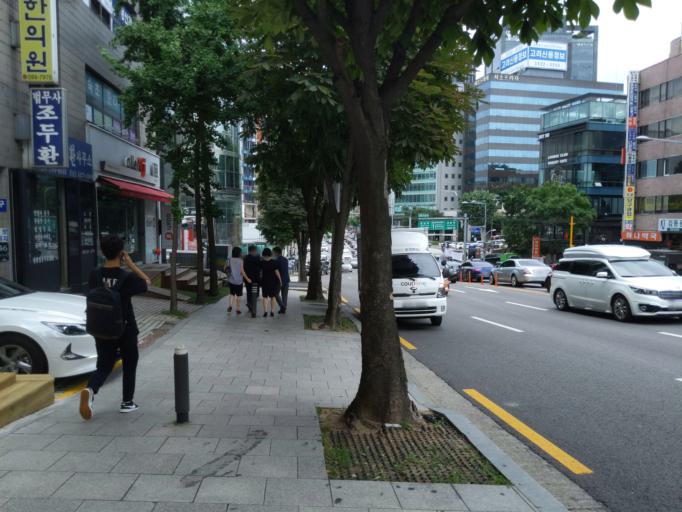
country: KR
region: Seoul
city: Seoul
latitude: 37.4948
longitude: 127.0134
